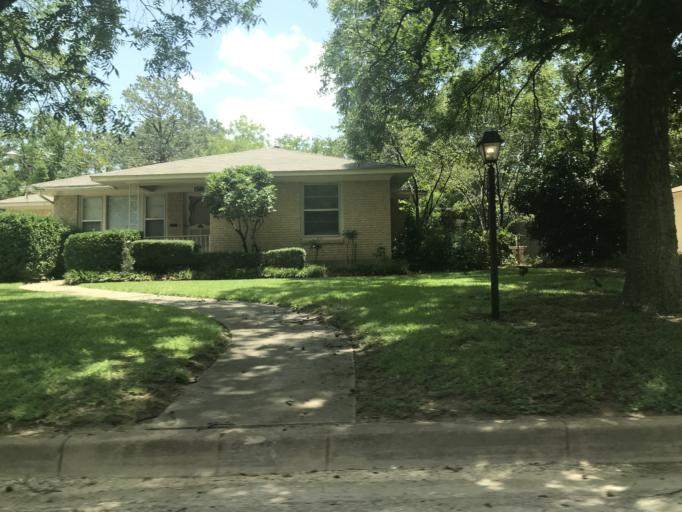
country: US
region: Texas
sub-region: Taylor County
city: Abilene
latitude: 32.4668
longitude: -99.7160
